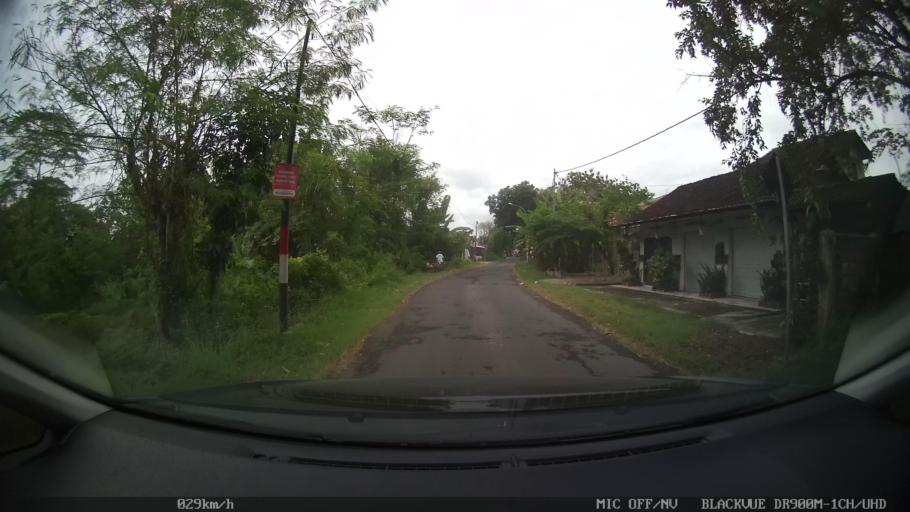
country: ID
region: Daerah Istimewa Yogyakarta
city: Sewon
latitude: -7.8580
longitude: 110.3981
